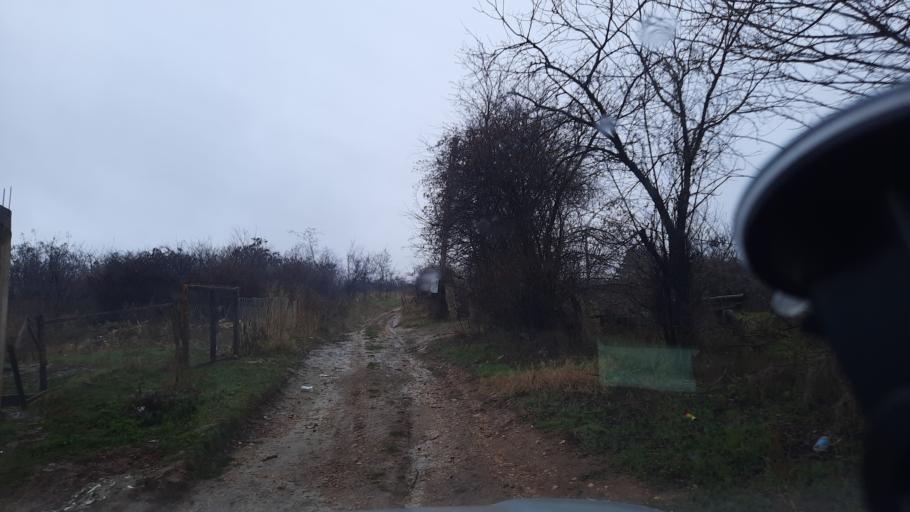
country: MK
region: Opstina Lipkovo
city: Matejche
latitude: 42.1225
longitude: 21.6006
